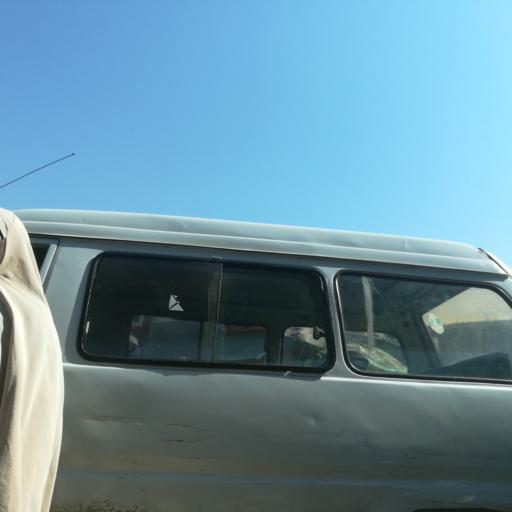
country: NG
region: Kano
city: Kano
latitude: 12.0109
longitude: 8.5349
